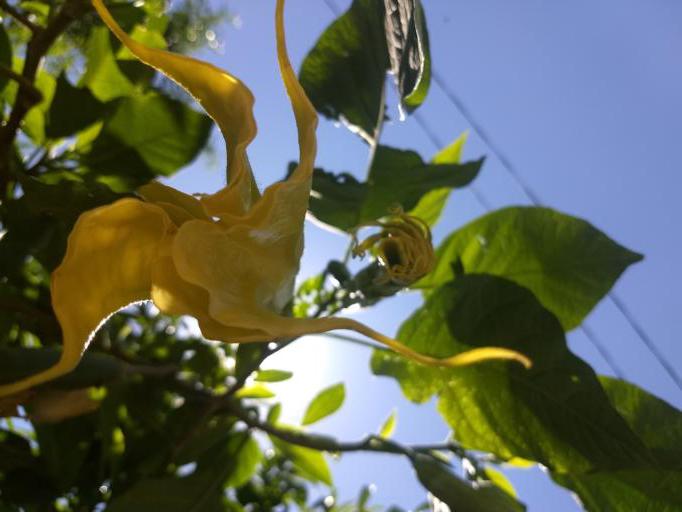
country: MX
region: Puebla
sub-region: Cuetzalan del Progreso
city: Cuauhtamazaco
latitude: 20.0133
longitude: -97.5025
